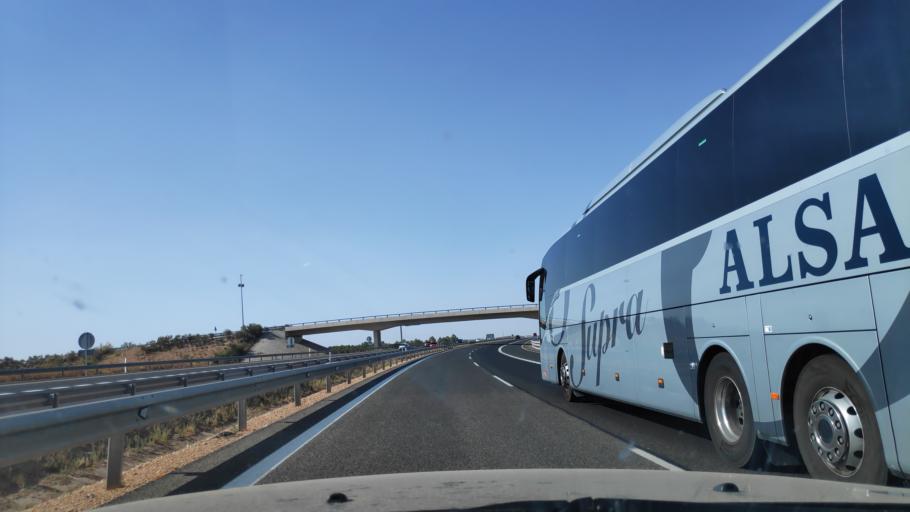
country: ES
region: Castille-La Mancha
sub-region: Provincia de Albacete
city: La Gineta
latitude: 39.1059
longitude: -1.9849
